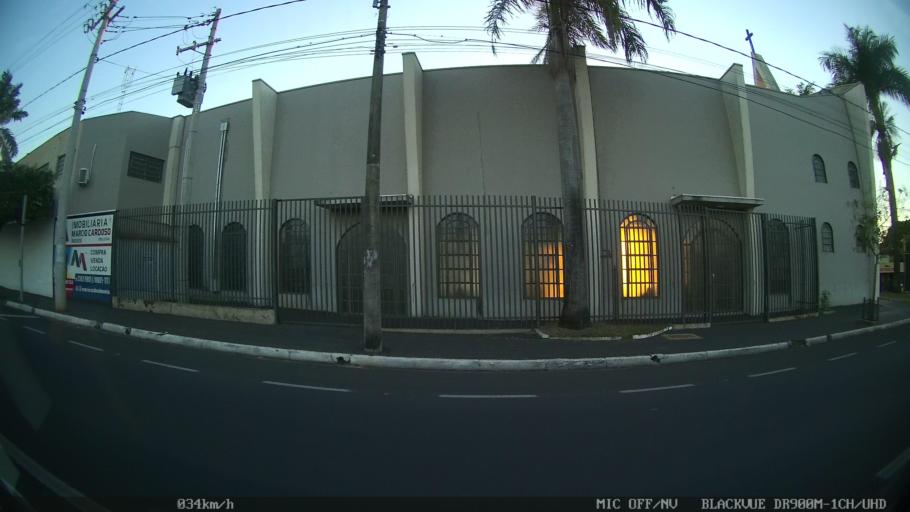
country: BR
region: Sao Paulo
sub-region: Sao Jose Do Rio Preto
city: Sao Jose do Rio Preto
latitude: -20.7910
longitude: -49.3446
